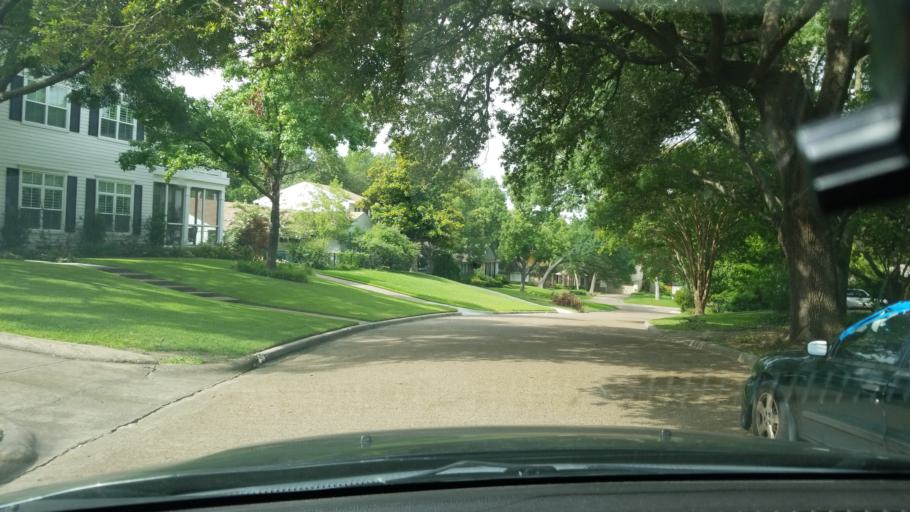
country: US
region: Texas
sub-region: Dallas County
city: Highland Park
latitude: 32.8278
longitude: -96.7131
